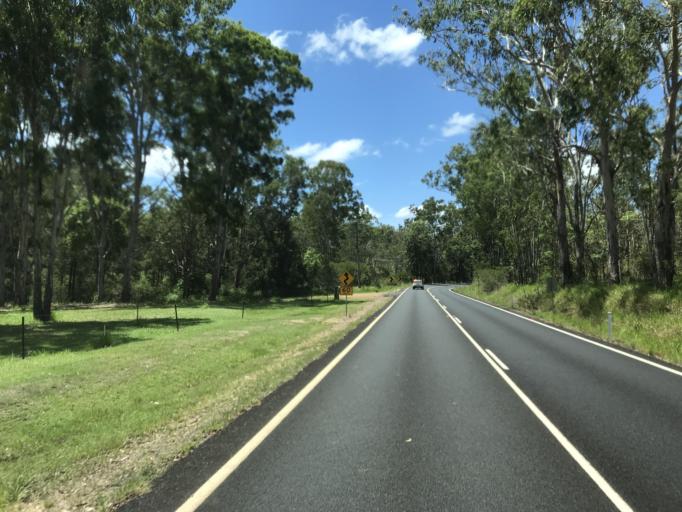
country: AU
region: Queensland
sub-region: Tablelands
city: Atherton
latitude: -17.4068
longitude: 145.3895
